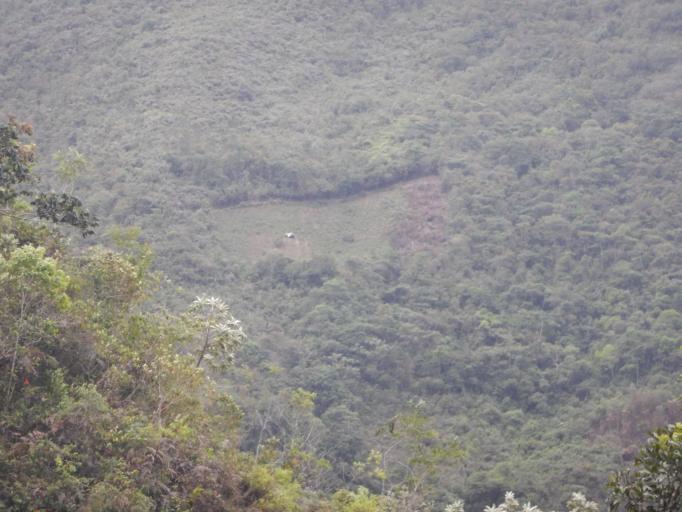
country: BO
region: La Paz
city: Coroico
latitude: -16.1118
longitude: -67.7822
